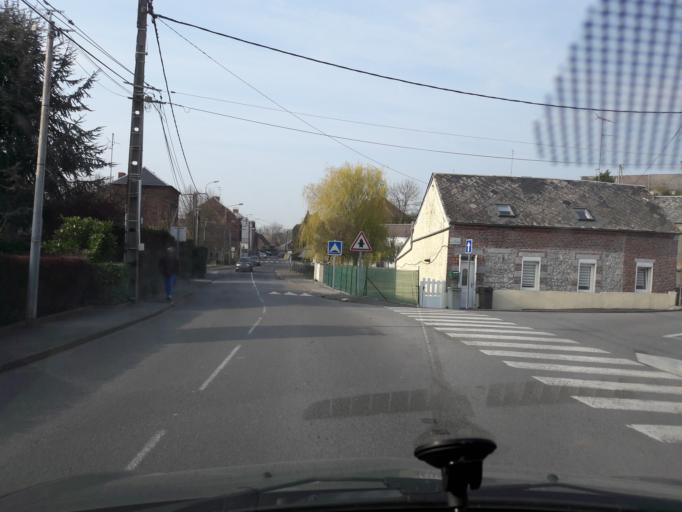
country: FR
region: Nord-Pas-de-Calais
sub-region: Departement du Nord
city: Rousies
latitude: 50.2688
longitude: 4.0049
